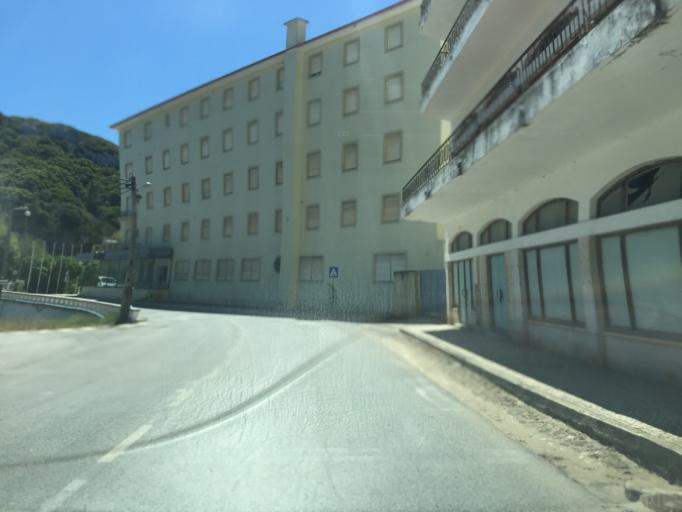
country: PT
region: Lisbon
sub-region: Torres Vedras
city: A dos Cunhados
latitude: 39.1831
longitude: -9.3264
